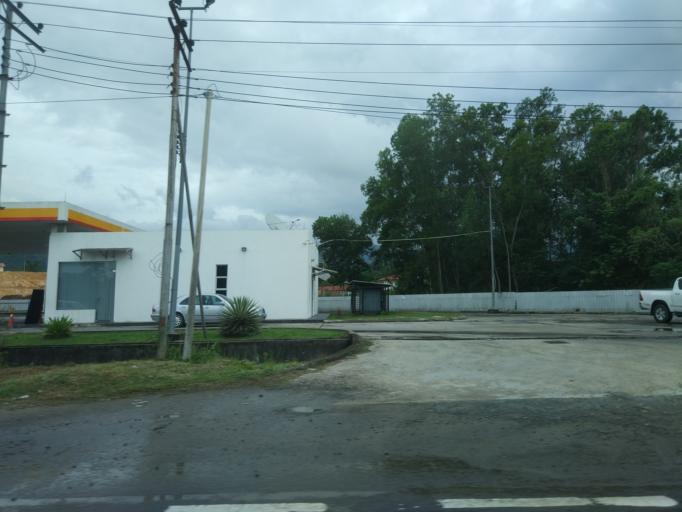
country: MY
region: Sabah
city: Kota Kinabalu
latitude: 6.0940
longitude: 116.1990
